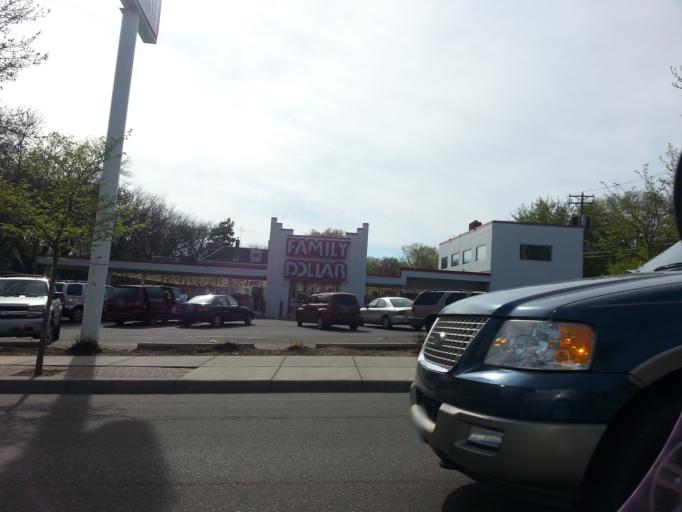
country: US
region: Minnesota
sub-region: Ramsey County
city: Saint Paul
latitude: 44.9732
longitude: -93.0735
